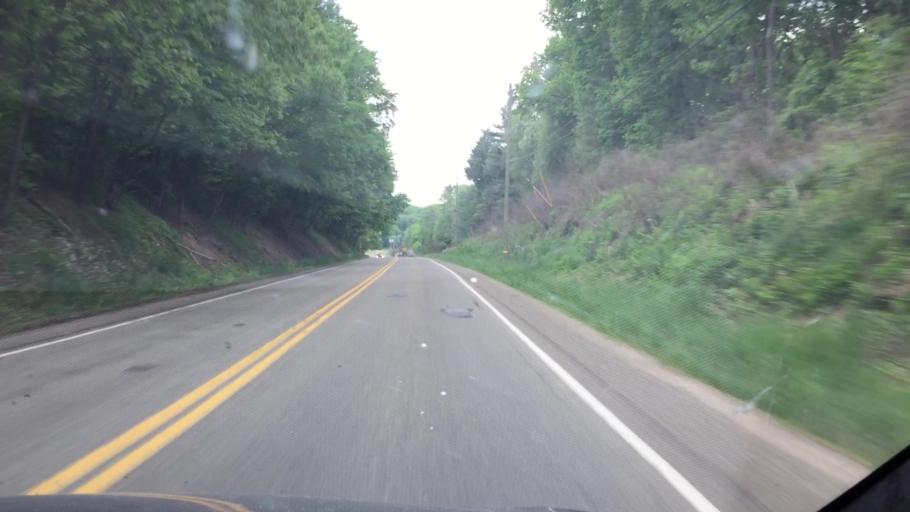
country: US
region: Pennsylvania
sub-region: Butler County
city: Slippery Rock
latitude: 41.0160
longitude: -80.0087
